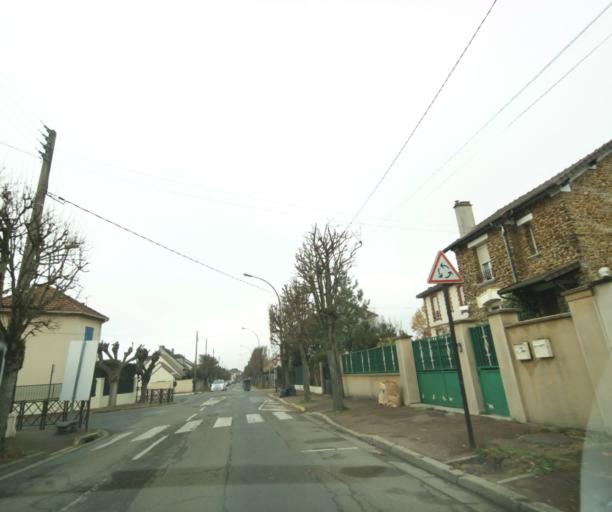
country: FR
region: Ile-de-France
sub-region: Departement de Seine-Saint-Denis
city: Livry-Gargan
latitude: 48.9255
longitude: 2.5314
